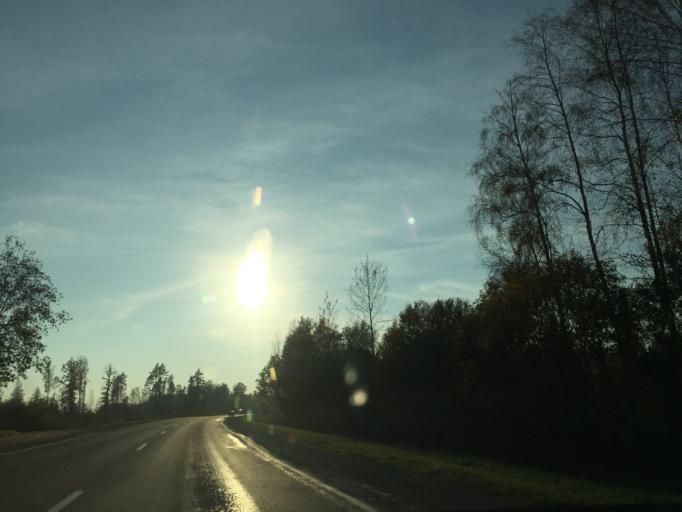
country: LV
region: Skrunda
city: Skrunda
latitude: 56.6325
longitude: 21.8473
